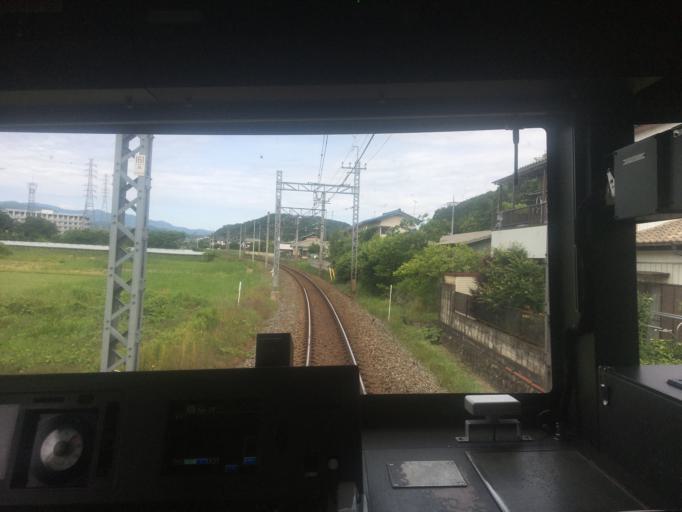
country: JP
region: Saitama
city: Ogawa
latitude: 36.0558
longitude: 139.2780
